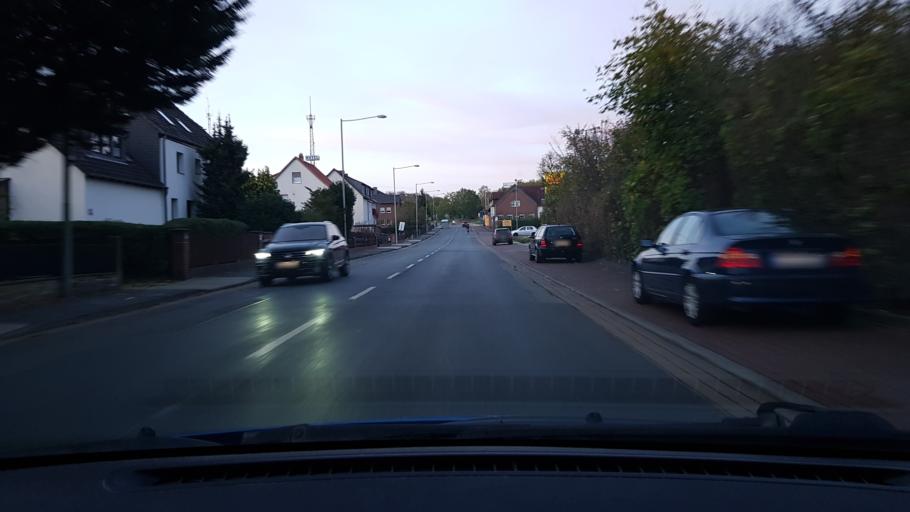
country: DE
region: Lower Saxony
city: Helmstedt
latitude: 52.2381
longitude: 11.0099
